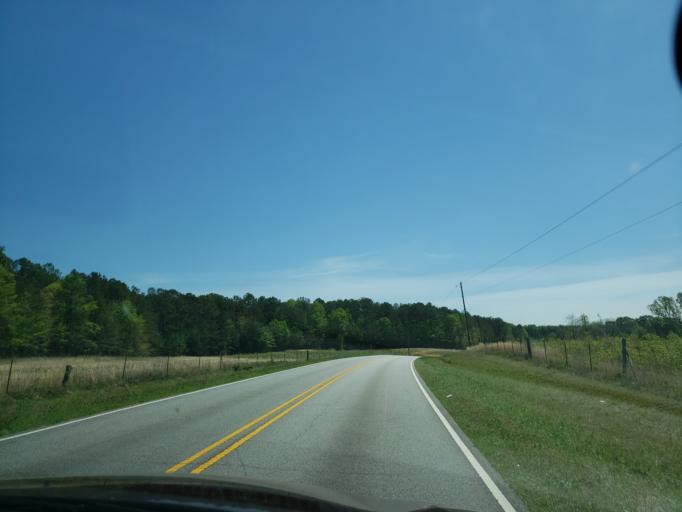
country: US
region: Alabama
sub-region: Tallapoosa County
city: Camp Hill
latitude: 32.7019
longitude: -85.6981
